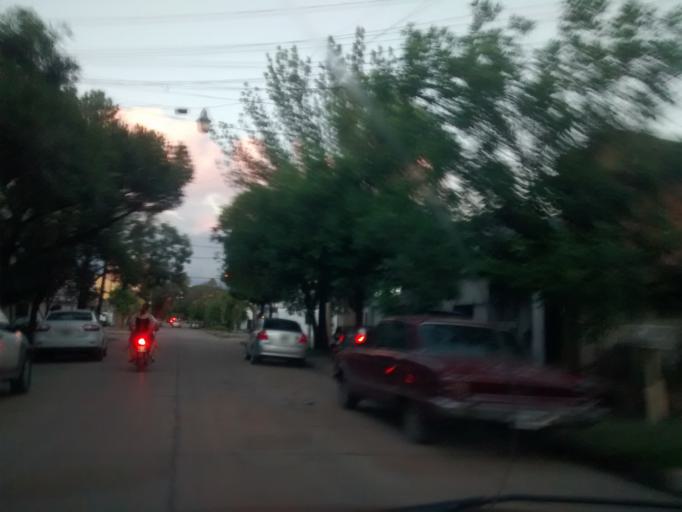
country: AR
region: Chaco
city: Resistencia
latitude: -27.4547
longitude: -58.9940
